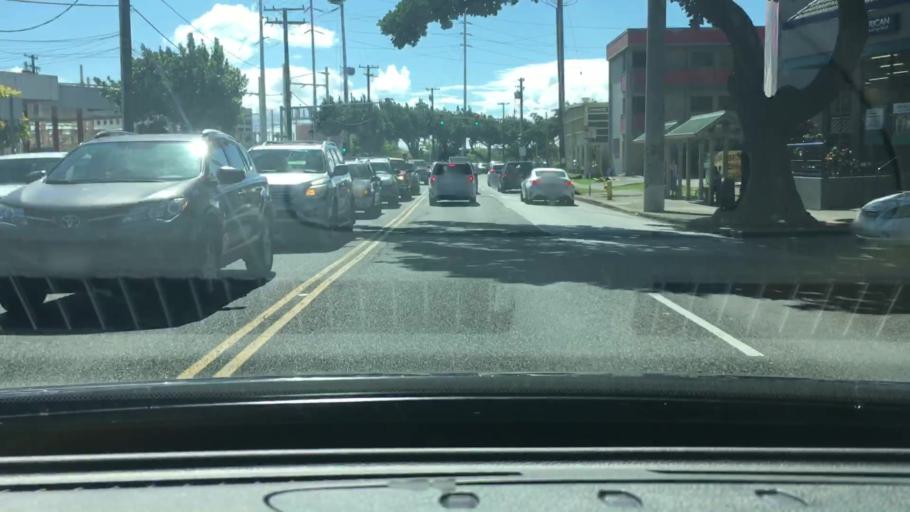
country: US
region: Hawaii
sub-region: Honolulu County
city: Honolulu
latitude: 21.3184
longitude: -157.8655
